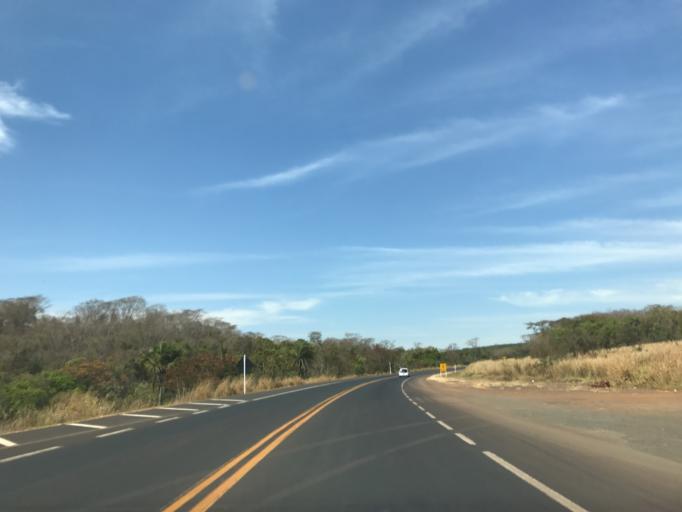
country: BR
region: Minas Gerais
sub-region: Monte Alegre De Minas
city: Monte Alegre de Minas
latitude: -19.0432
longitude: -49.0097
